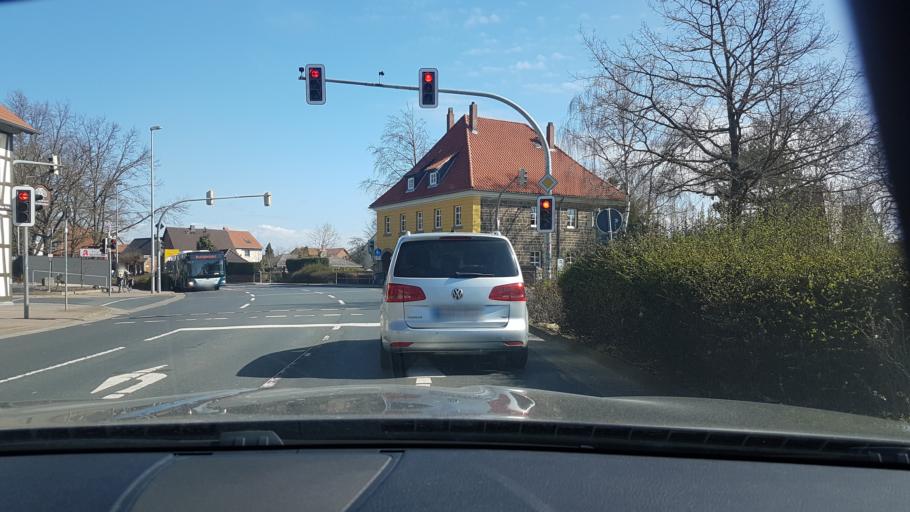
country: DE
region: Lower Saxony
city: Pattensen
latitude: 52.2613
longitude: 9.7639
